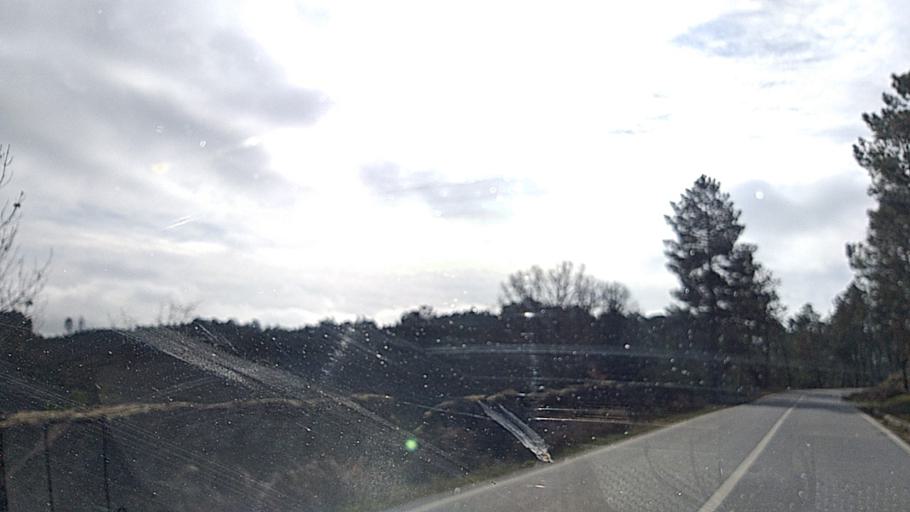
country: PT
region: Guarda
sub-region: Fornos de Algodres
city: Fornos de Algodres
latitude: 40.7073
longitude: -7.5651
